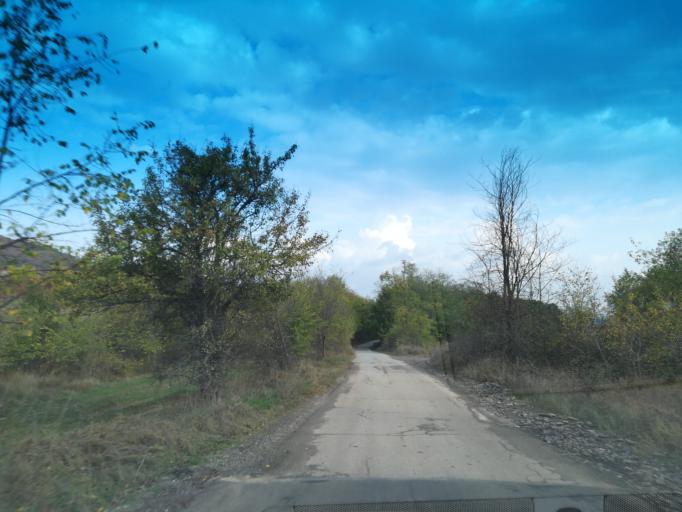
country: BG
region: Stara Zagora
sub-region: Obshtina Nikolaevo
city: Elkhovo
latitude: 42.3277
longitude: 25.4004
